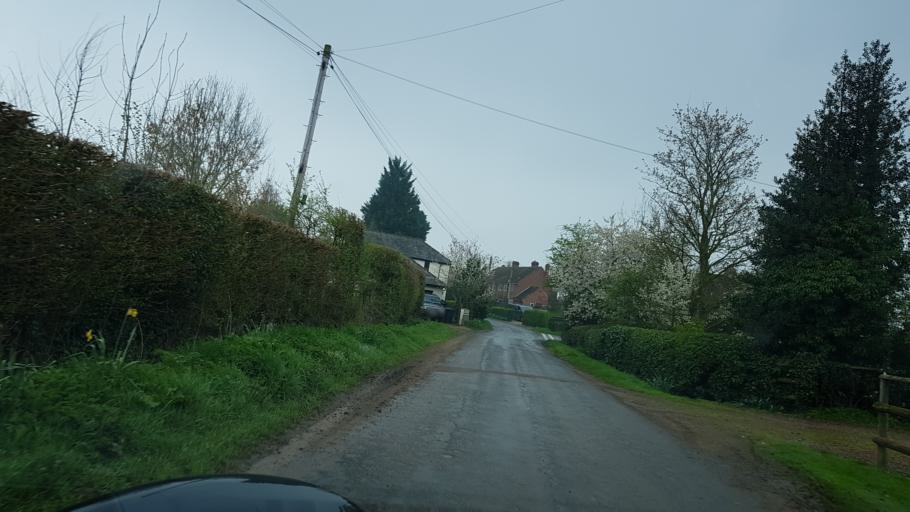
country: GB
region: England
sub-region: Herefordshire
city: Yatton
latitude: 52.0205
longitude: -2.5215
